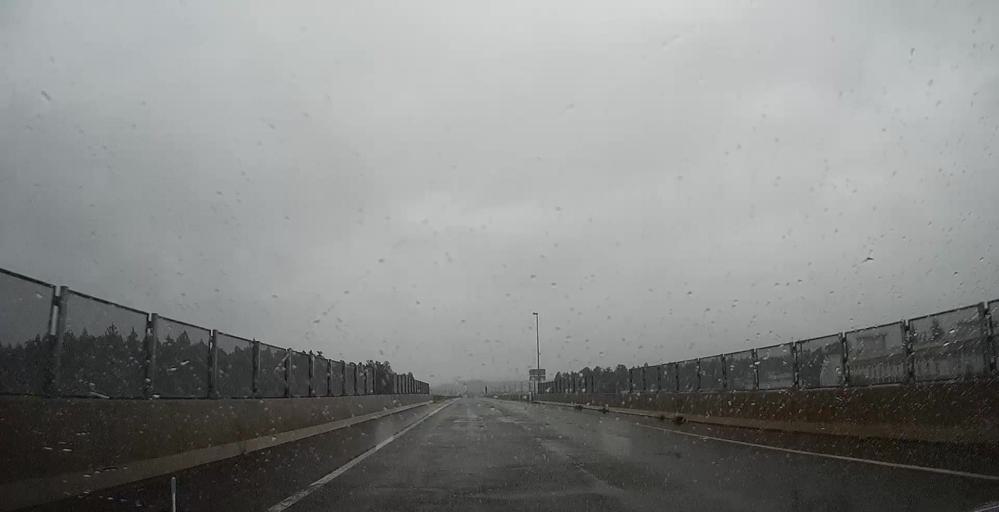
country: JP
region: Niigata
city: Murakami
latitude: 38.1062
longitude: 139.4355
